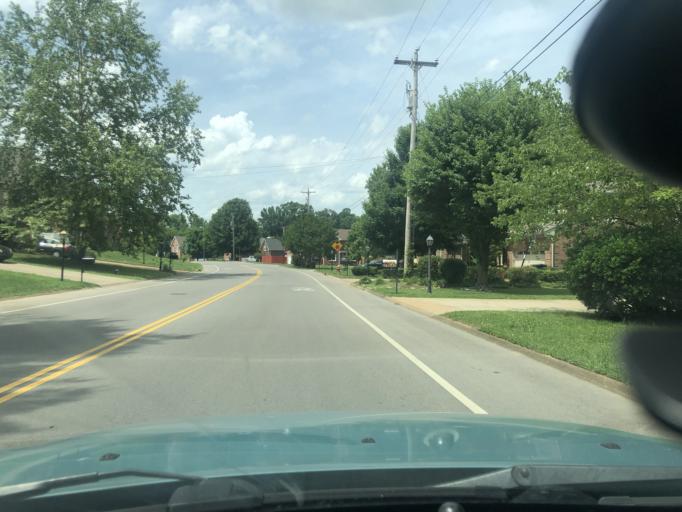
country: US
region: Tennessee
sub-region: Davidson County
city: Lakewood
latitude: 36.1316
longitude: -86.6375
